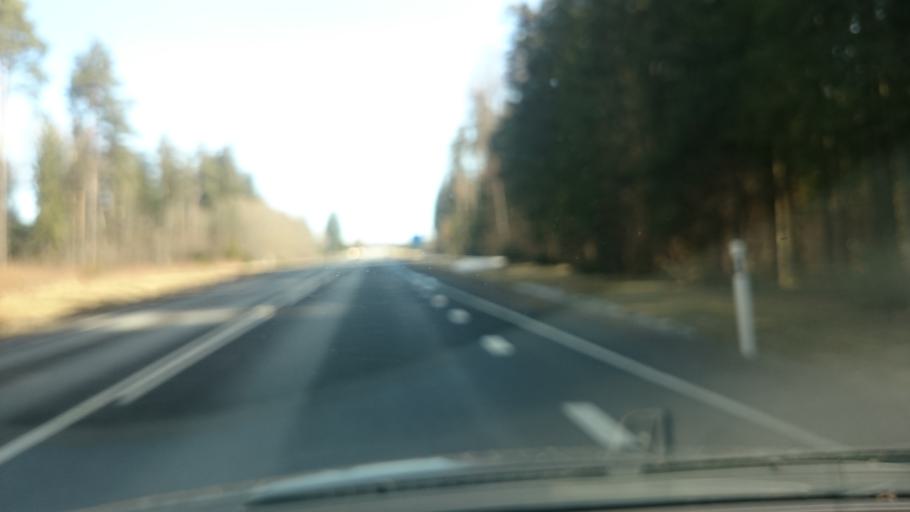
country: EE
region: Paernumaa
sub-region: Vaendra vald (alev)
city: Vandra
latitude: 58.6699
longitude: 25.0871
